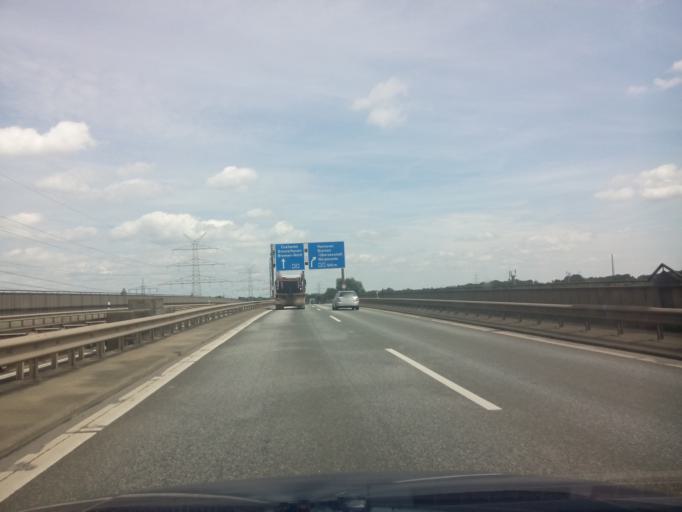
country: DE
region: Lower Saxony
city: Ritterhude
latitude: 53.1417
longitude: 8.7212
